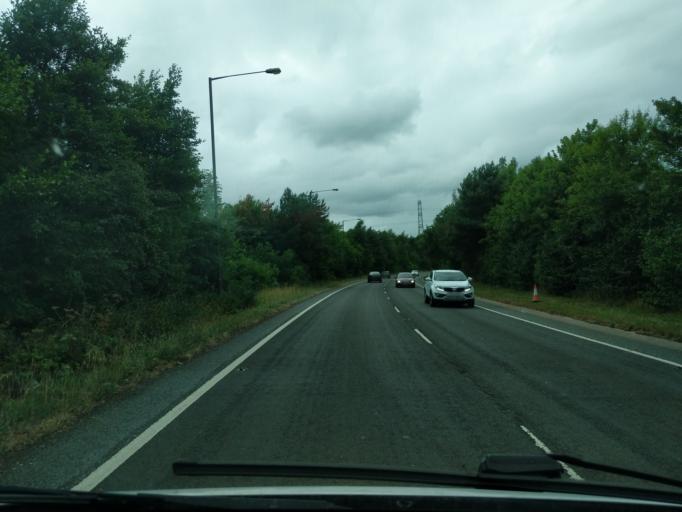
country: GB
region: England
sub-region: Cheshire West and Chester
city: Weaverham
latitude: 53.2612
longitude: -2.5895
